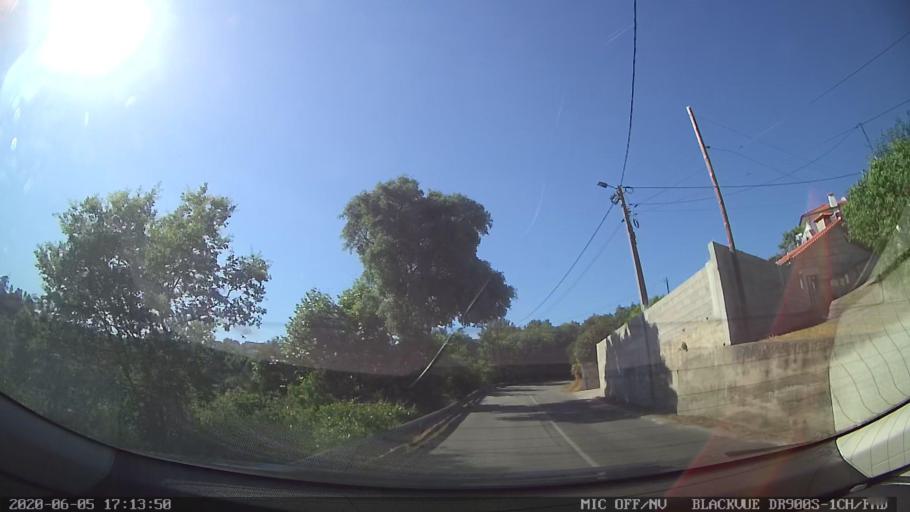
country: PT
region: Porto
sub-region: Amarante
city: Amarante
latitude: 41.2715
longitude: -8.0951
